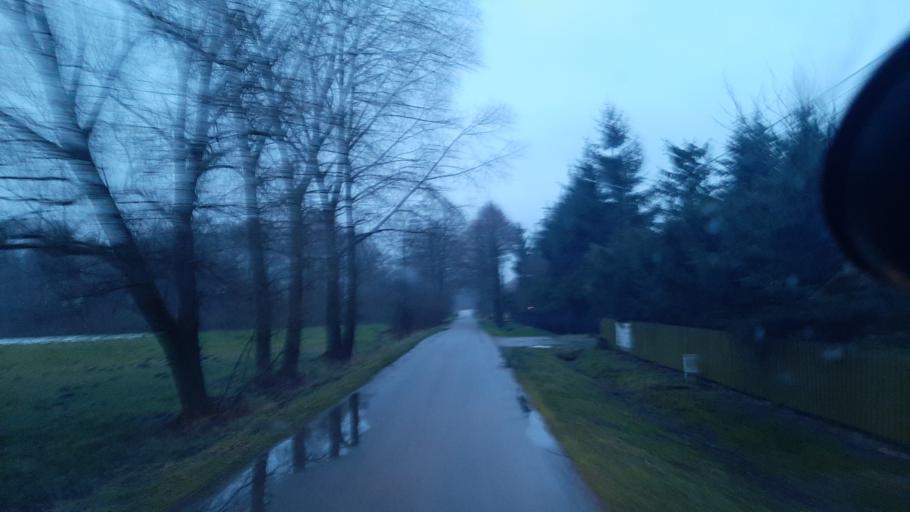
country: PL
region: Lublin Voivodeship
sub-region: Powiat lubelski
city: Jastkow
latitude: 51.3888
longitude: 22.4134
